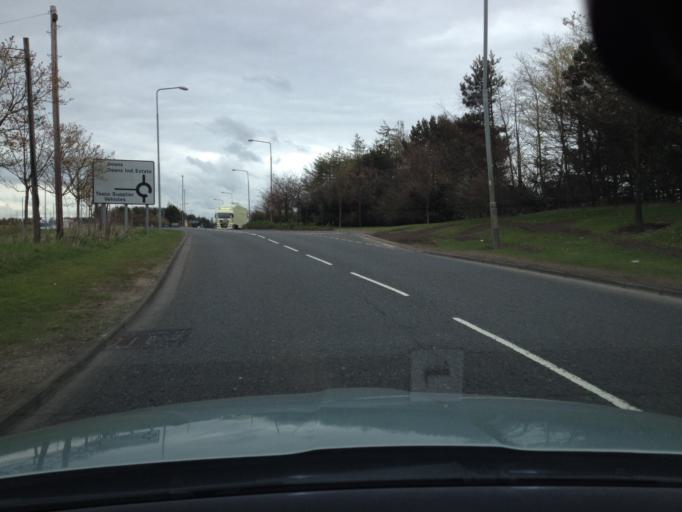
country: GB
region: Scotland
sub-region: West Lothian
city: West Calder
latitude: 55.9018
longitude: -3.5839
